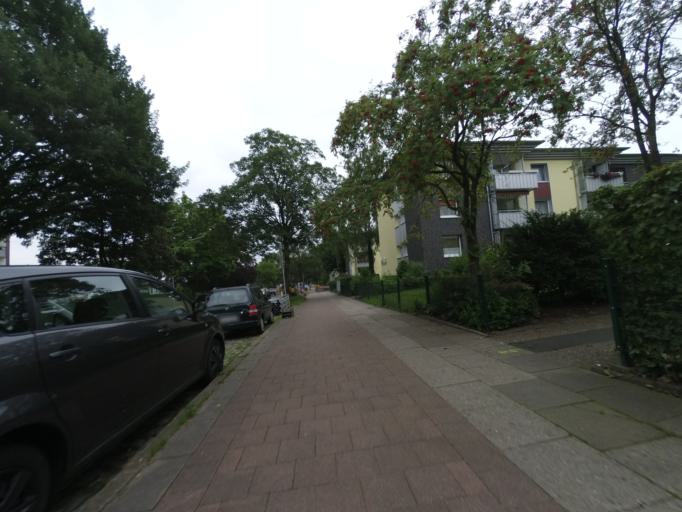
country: DE
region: Hamburg
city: Bergedorf
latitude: 53.5023
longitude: 10.1946
